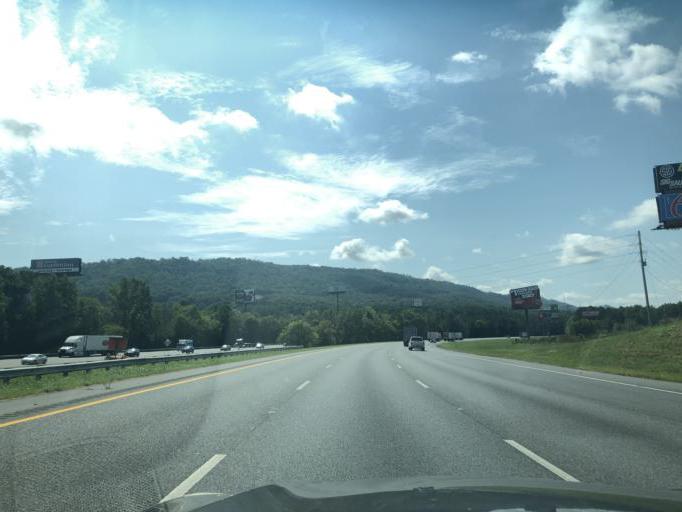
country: US
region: Georgia
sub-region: Whitfield County
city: Varnell
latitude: 34.8569
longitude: -85.0200
